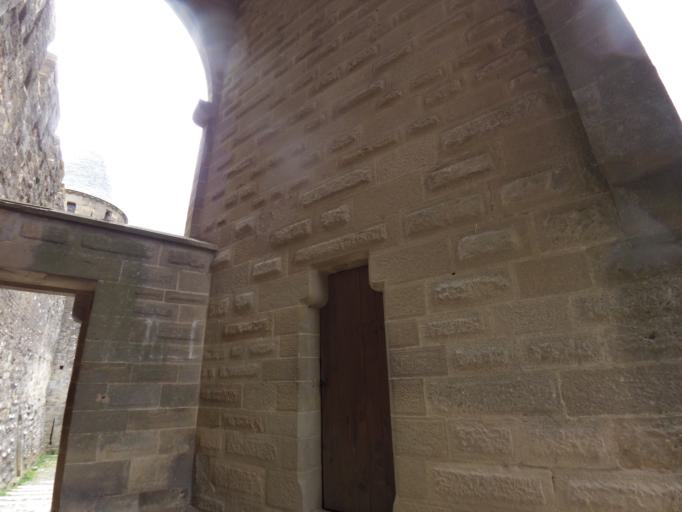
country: FR
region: Languedoc-Roussillon
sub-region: Departement de l'Aude
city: Carcassonne
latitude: 43.2069
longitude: 2.3628
